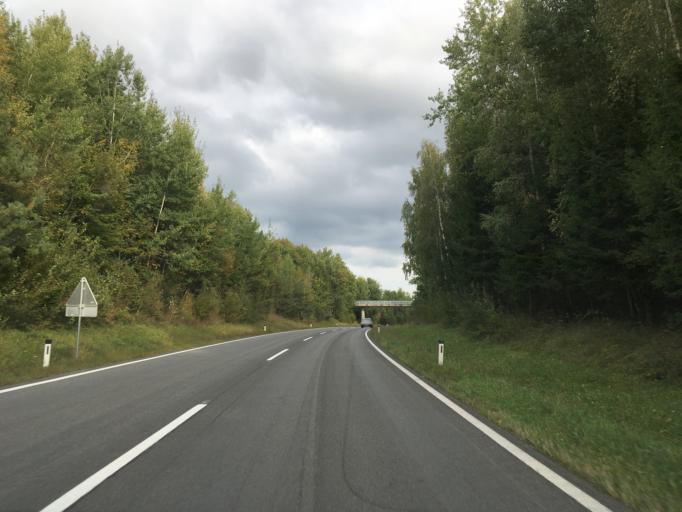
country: AT
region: Styria
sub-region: Politischer Bezirk Hartberg-Fuerstenfeld
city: Dechantskirchen
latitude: 47.4171
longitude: 16.0312
